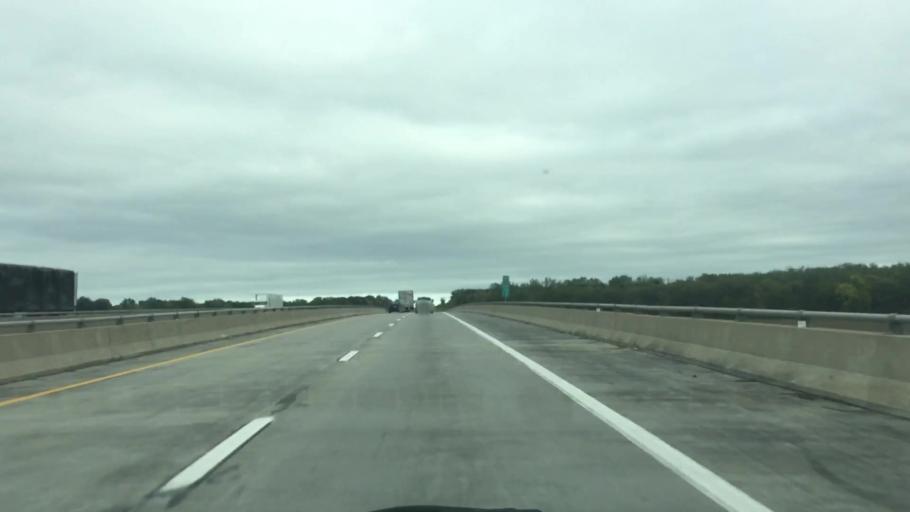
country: US
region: Missouri
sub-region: Daviess County
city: Gallatin
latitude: 40.0467
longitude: -94.0946
